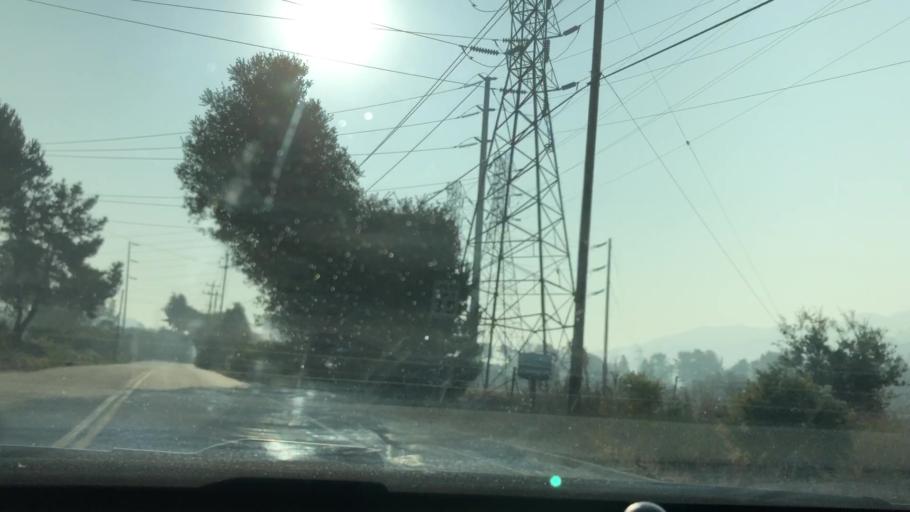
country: US
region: California
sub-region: Contra Costa County
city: Orinda
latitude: 37.9054
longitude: -122.2100
